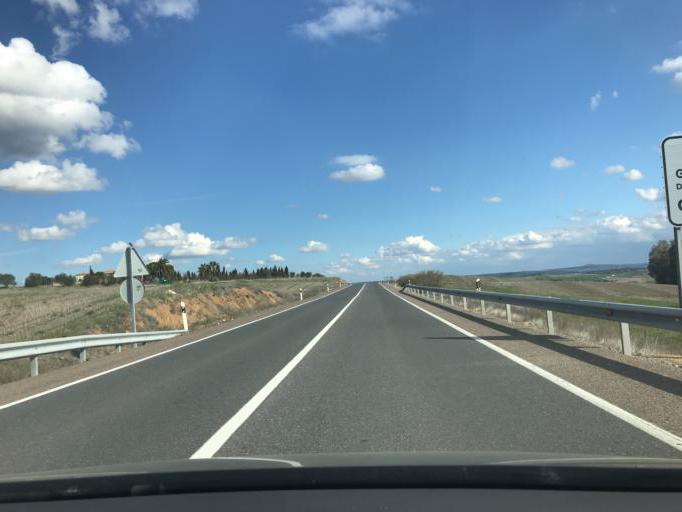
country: ES
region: Extremadura
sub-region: Provincia de Badajoz
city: Azuaga
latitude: 38.2766
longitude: -5.6742
